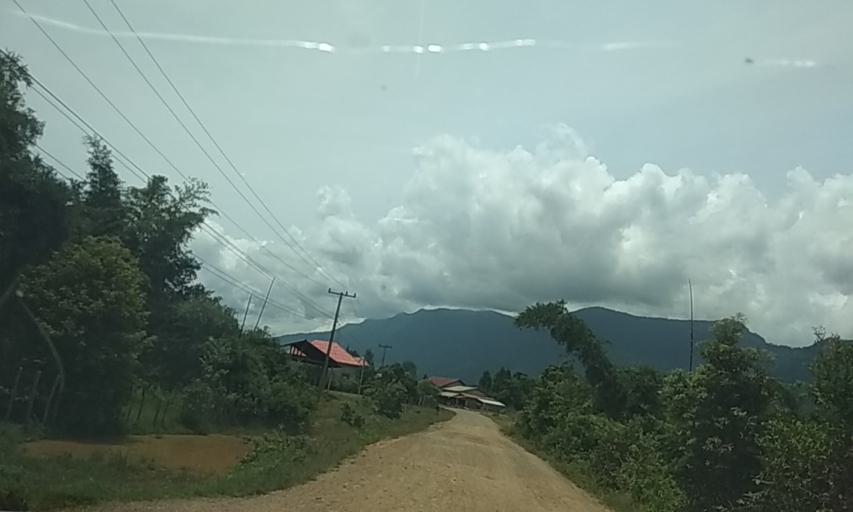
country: LA
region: Bolikhamxai
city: Ban Nahin
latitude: 18.1417
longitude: 104.7574
